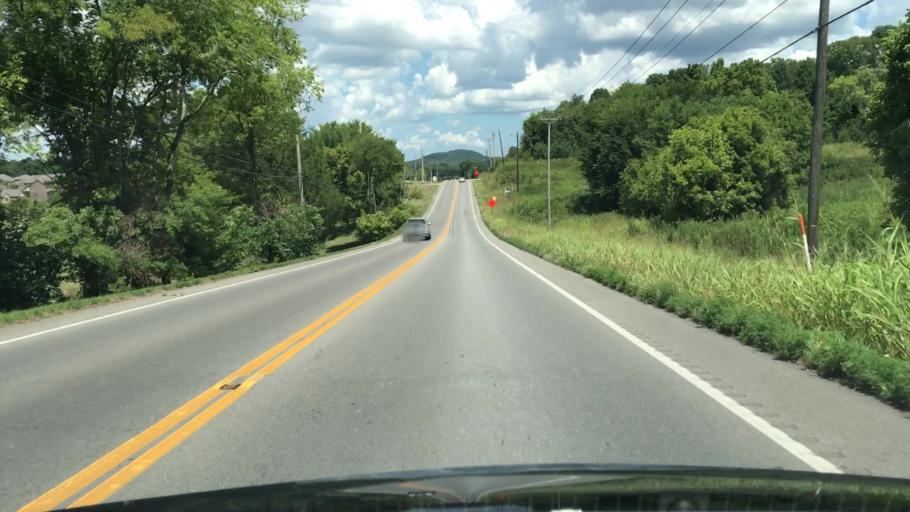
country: US
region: Tennessee
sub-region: Williamson County
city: Nolensville
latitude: 35.8742
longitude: -86.6604
